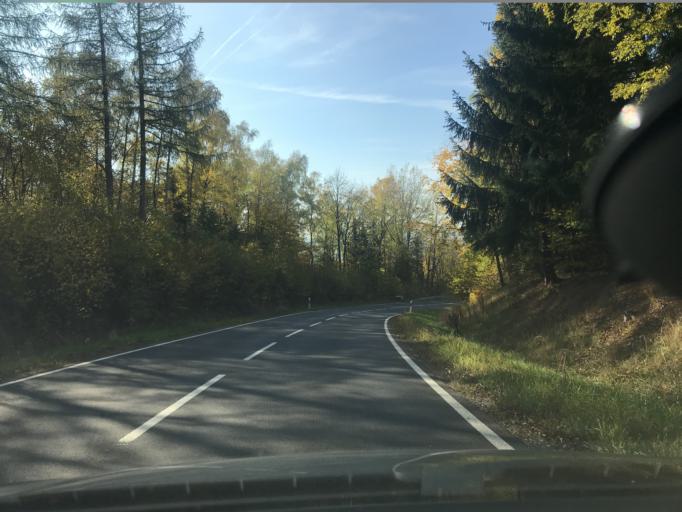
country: DE
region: Hesse
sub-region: Regierungsbezirk Kassel
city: Grossalmerode
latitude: 51.2093
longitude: 9.8303
